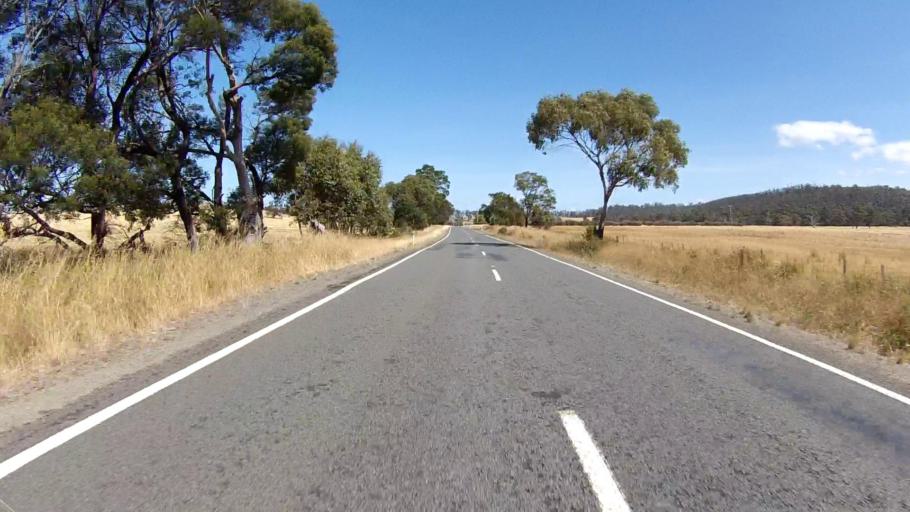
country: AU
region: Tasmania
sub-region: Sorell
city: Sorell
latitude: -42.4552
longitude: 147.9287
